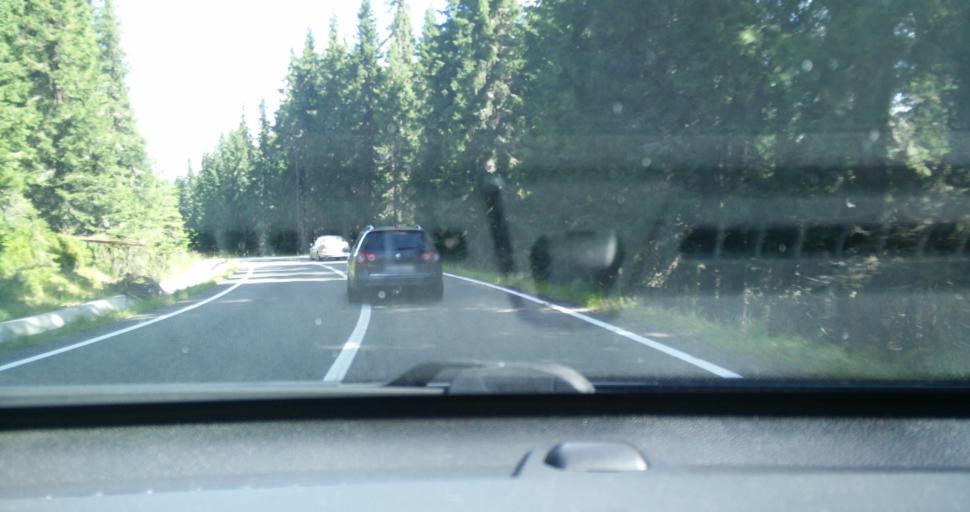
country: RO
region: Hunedoara
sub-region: Oras Petrila
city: Petrila
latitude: 45.4751
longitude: 23.6404
